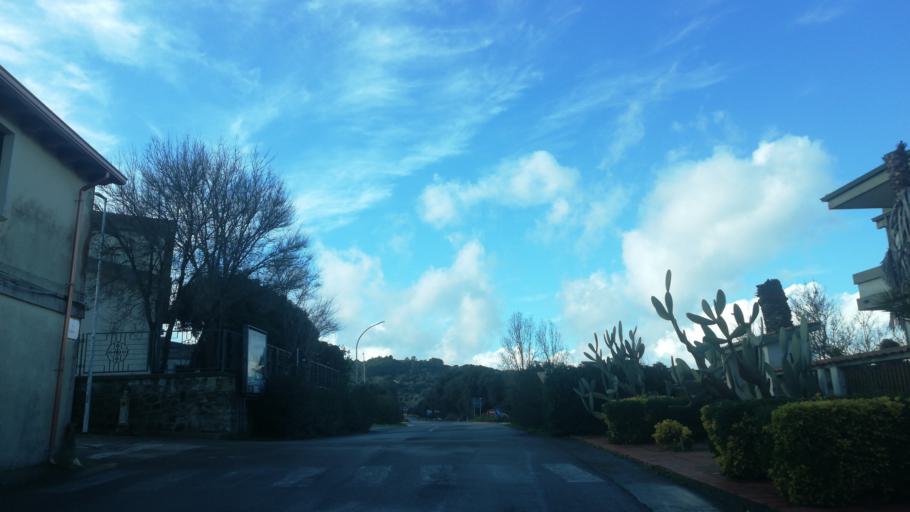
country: IT
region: Sardinia
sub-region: Provincia di Medio Campidano
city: Villanovaforru
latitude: 39.6330
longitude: 8.8648
